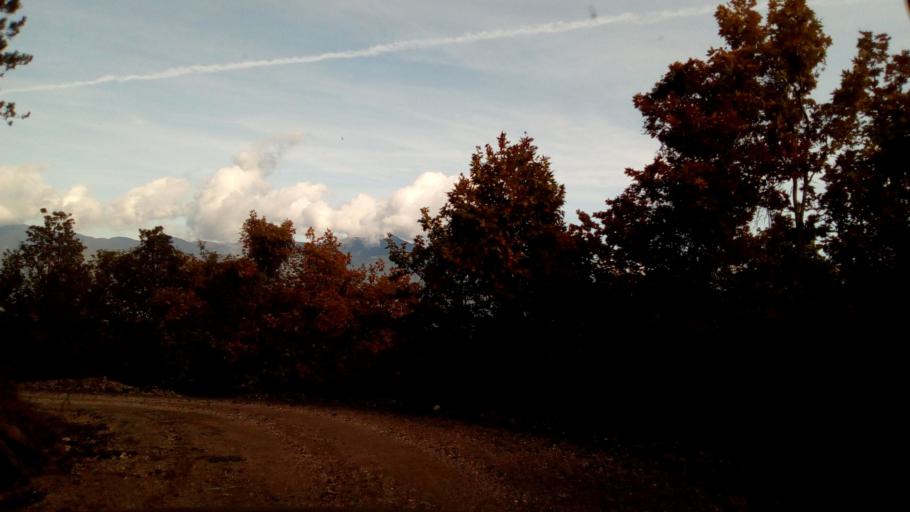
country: GR
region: West Greece
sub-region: Nomos Achaias
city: Kamarai
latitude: 38.4789
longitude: 22.0246
